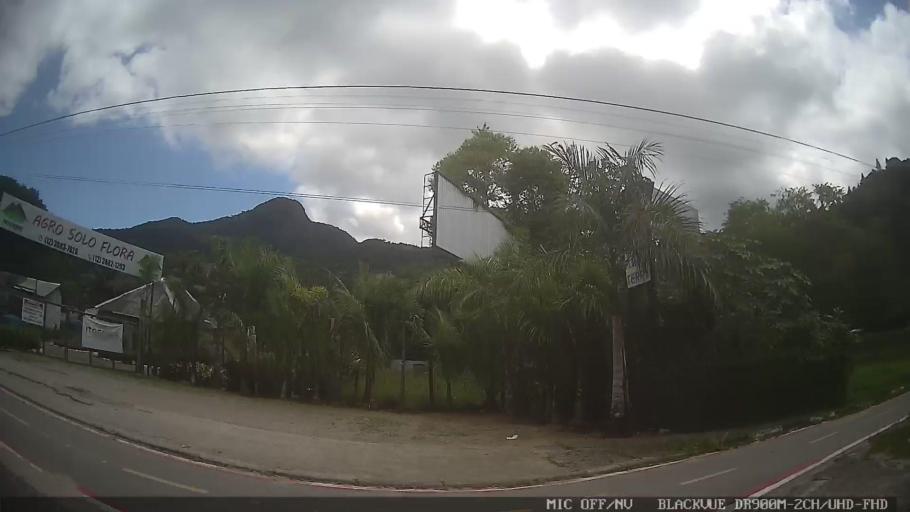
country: BR
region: Sao Paulo
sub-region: Caraguatatuba
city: Caraguatatuba
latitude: -23.6115
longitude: -45.4306
